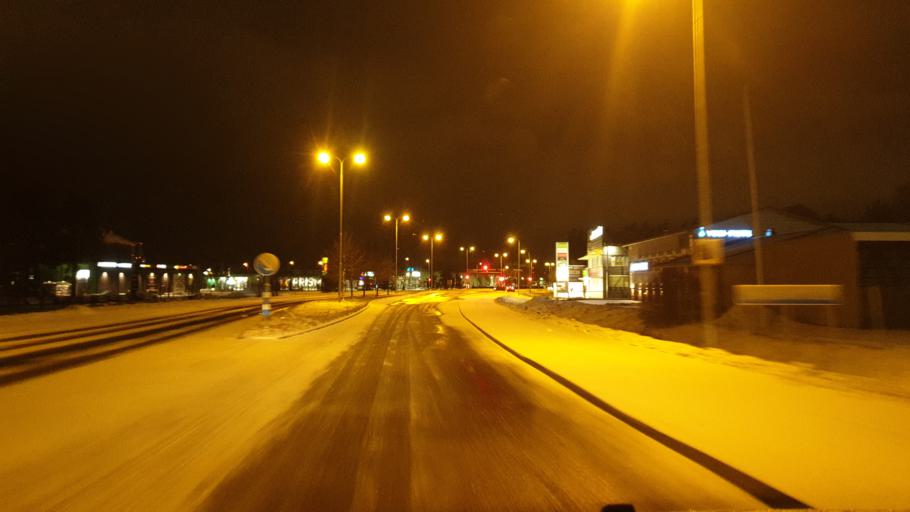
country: FI
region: Northern Ostrobothnia
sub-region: Oulu
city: Oulu
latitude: 64.9905
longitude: 25.4668
